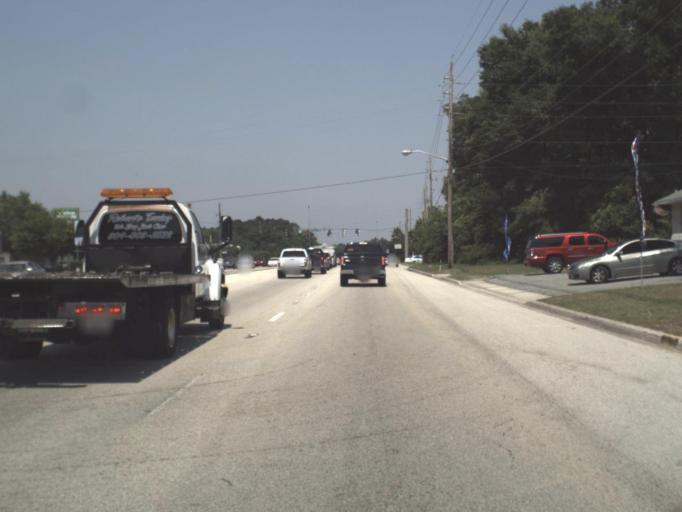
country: US
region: Florida
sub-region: Clay County
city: Bellair-Meadowbrook Terrace
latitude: 30.2941
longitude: -81.7779
